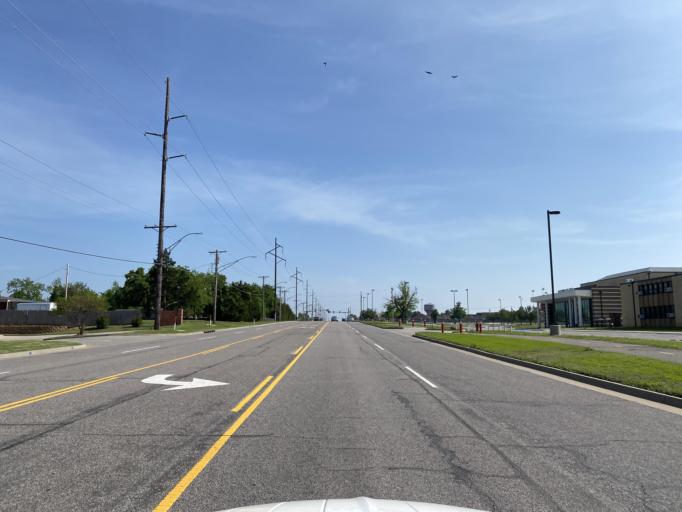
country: US
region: Oklahoma
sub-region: Oklahoma County
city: Midwest City
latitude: 35.4448
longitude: -97.3532
